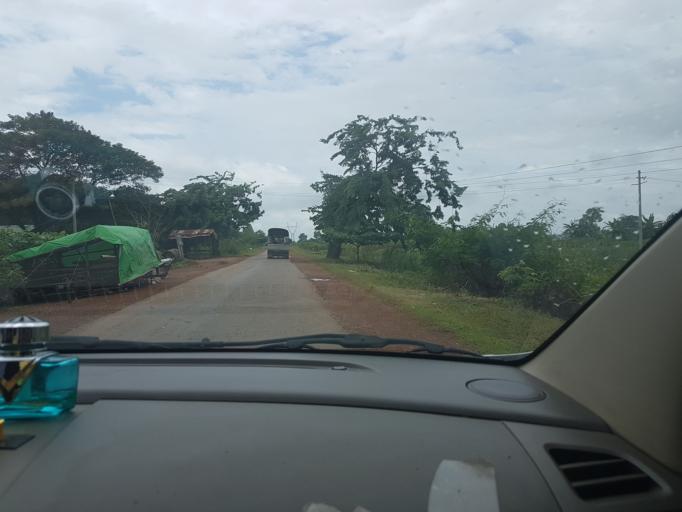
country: MM
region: Bago
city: Nyaunglebin
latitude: 17.9314
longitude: 96.8159
